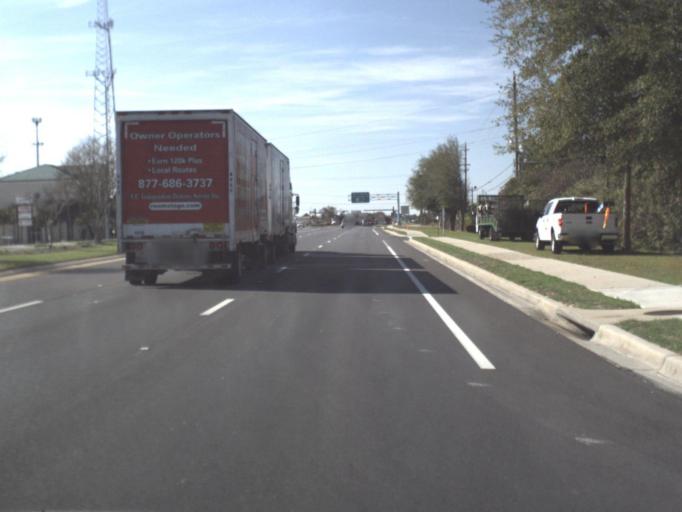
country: US
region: Florida
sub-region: Bay County
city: Laguna Beach
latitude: 30.2287
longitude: -85.8834
